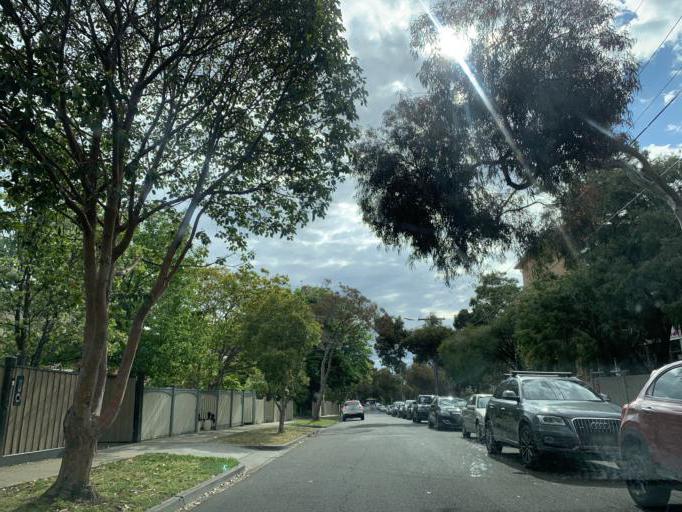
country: AU
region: Victoria
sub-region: Bayside
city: Hampton
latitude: -37.9318
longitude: 145.0073
